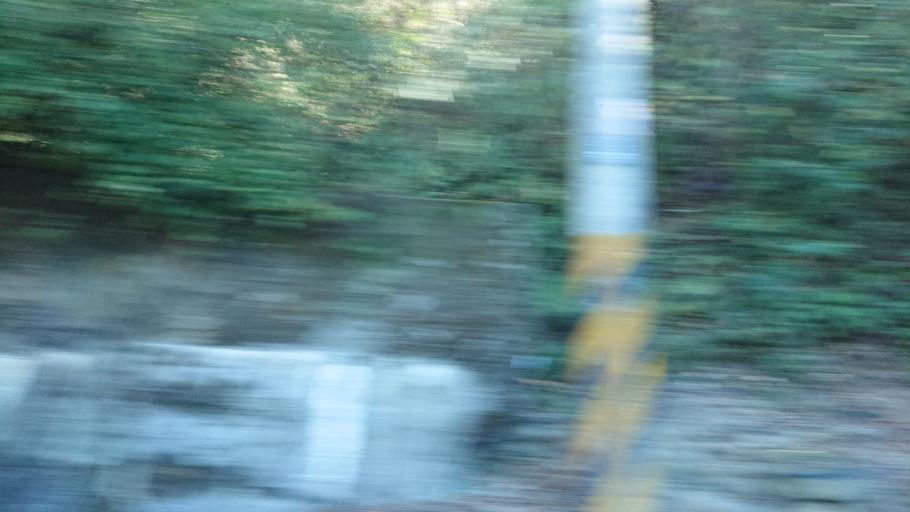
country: TW
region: Taiwan
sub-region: Hualien
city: Hualian
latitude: 24.3519
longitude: 121.3248
